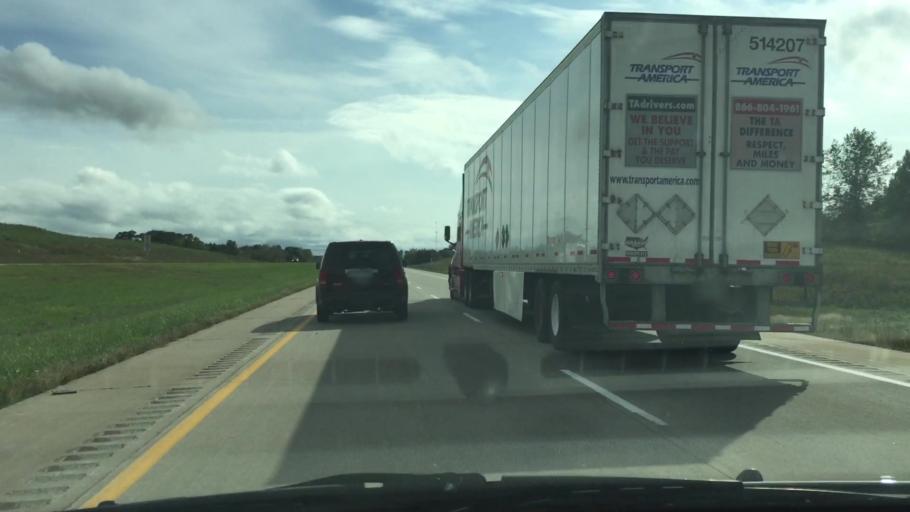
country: US
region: Iowa
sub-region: Decatur County
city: Leon
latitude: 40.8814
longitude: -93.8020
